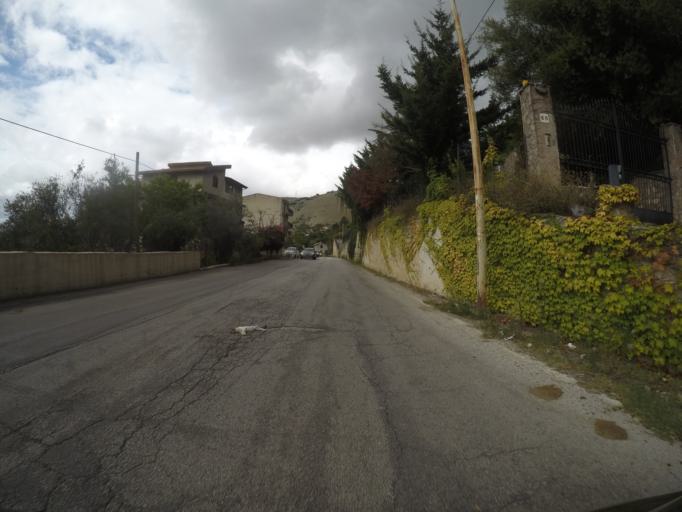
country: IT
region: Sicily
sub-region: Palermo
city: Montelepre
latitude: 38.0935
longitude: 13.1694
